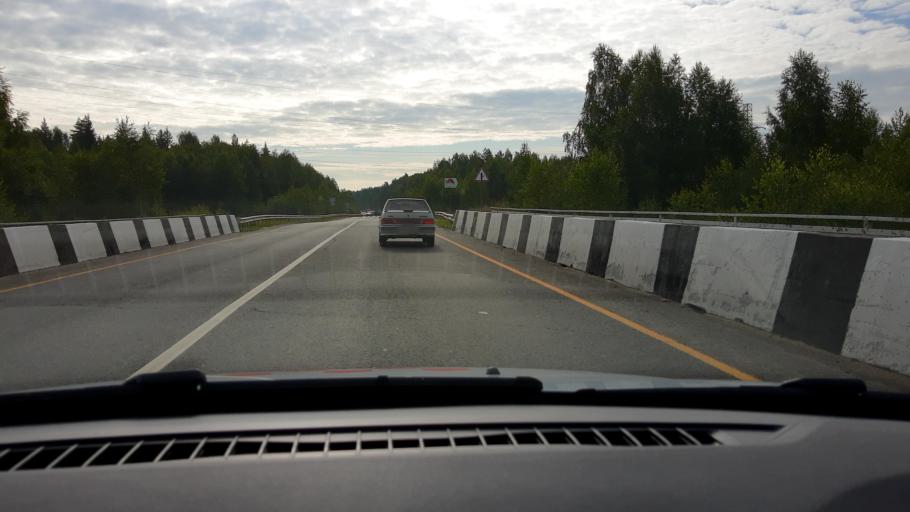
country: RU
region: Nizjnij Novgorod
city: Semenov
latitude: 56.8215
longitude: 44.5100
